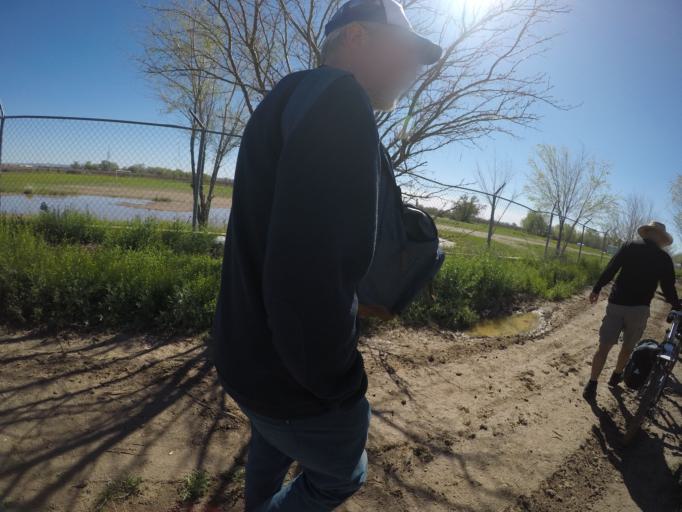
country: US
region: Texas
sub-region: El Paso County
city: Socorro
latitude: 31.6381
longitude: -106.3349
